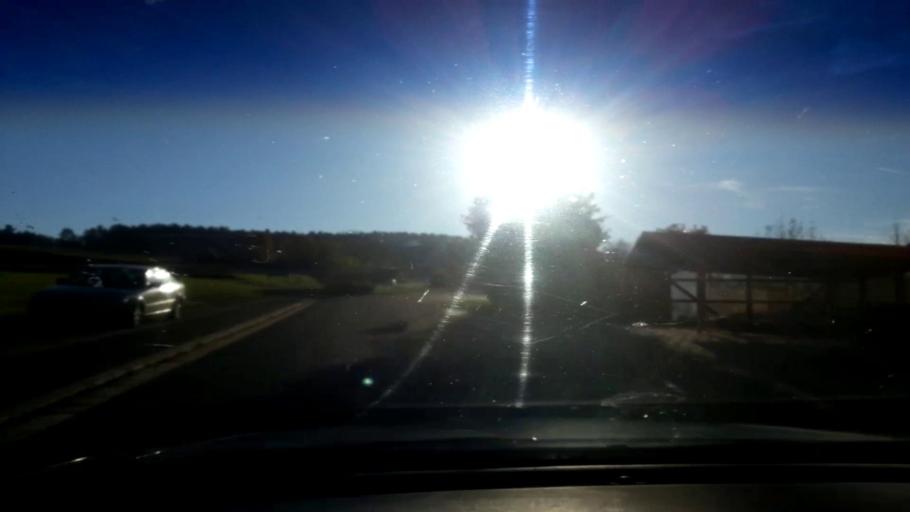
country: DE
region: Bavaria
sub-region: Upper Franconia
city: Heiligenstadt
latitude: 49.8625
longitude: 11.1652
